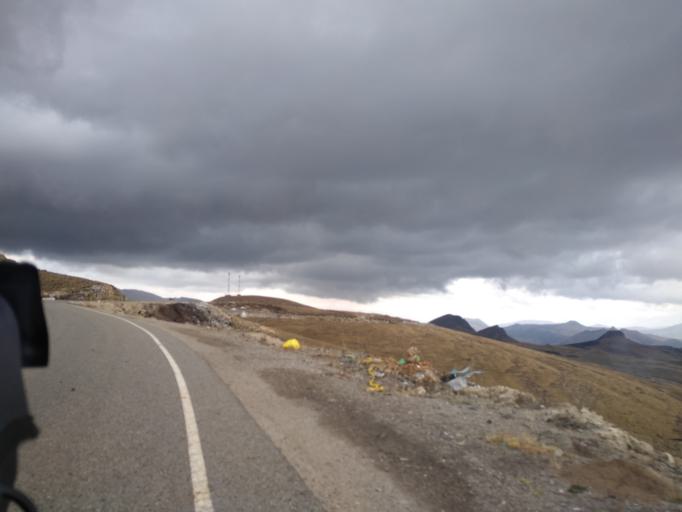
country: PE
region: La Libertad
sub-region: Provincia de Santiago de Chuco
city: Quiruvilca
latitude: -7.9926
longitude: -78.3028
